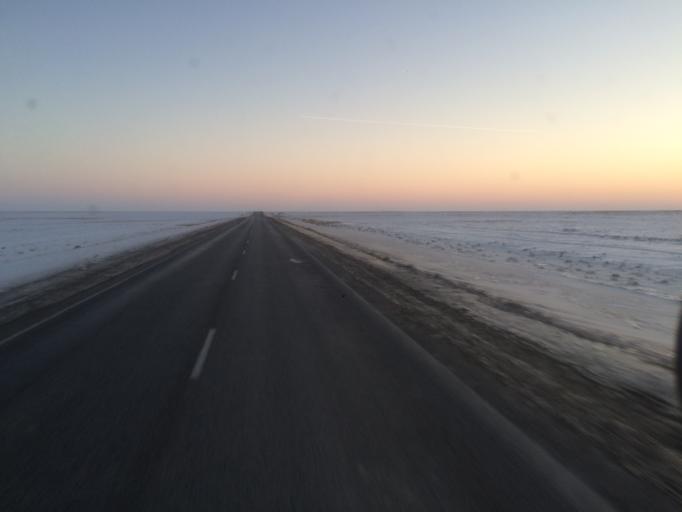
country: KZ
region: Qyzylorda
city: Sekseuil
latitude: 47.4192
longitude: 61.5383
